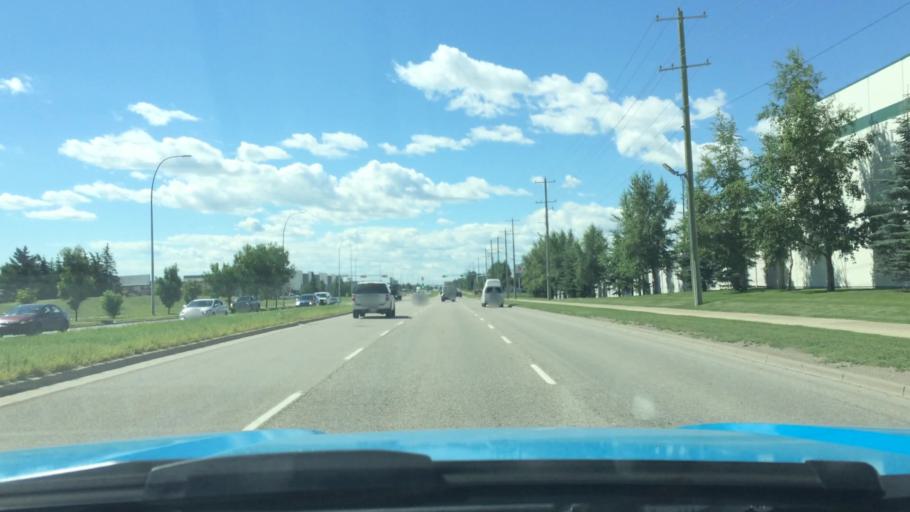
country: CA
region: Alberta
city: Calgary
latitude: 50.9960
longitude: -113.9587
